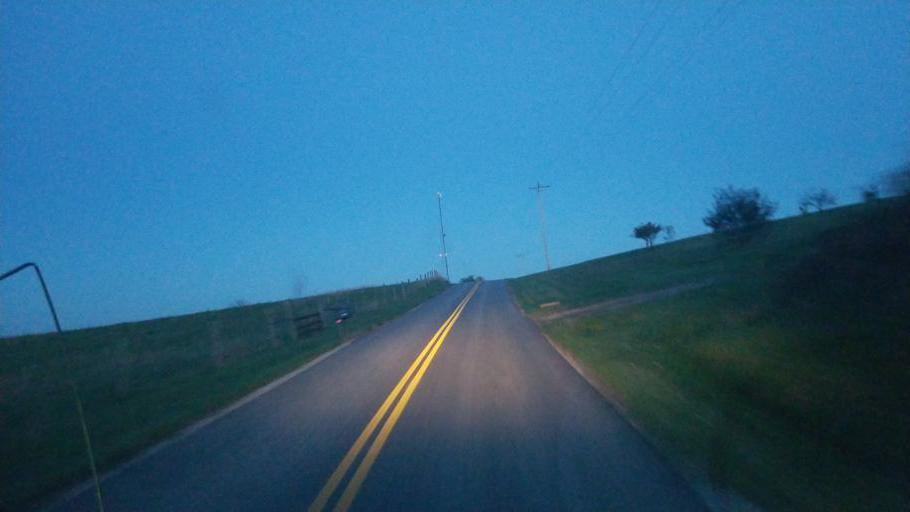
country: US
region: Ohio
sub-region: Perry County
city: Somerset
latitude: 39.8607
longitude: -82.2381
